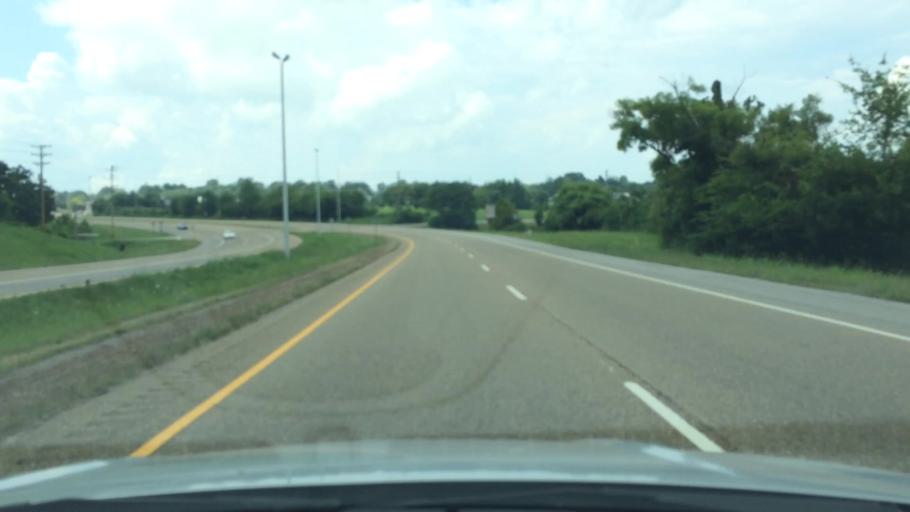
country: US
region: Tennessee
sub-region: Hamblen County
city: Morristown
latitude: 36.1746
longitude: -83.3885
